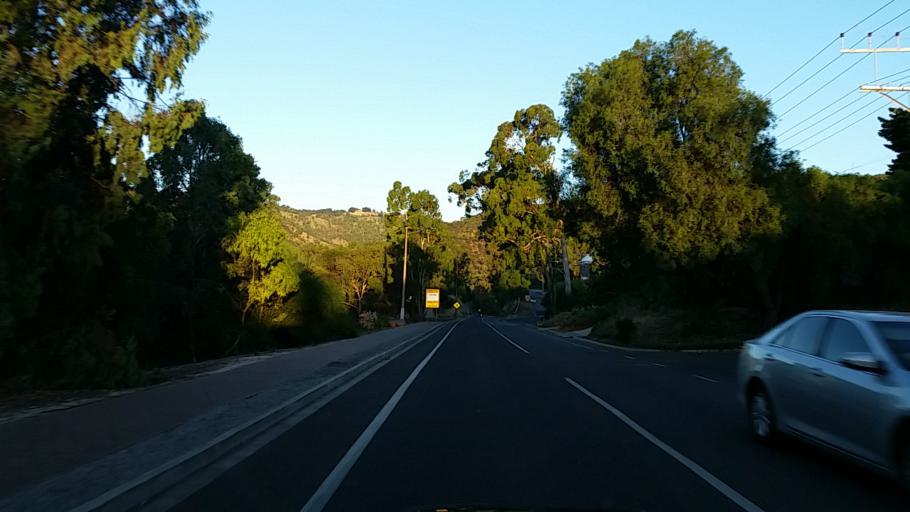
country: AU
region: South Australia
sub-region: Campbelltown
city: Athelstone
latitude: -34.8642
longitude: 138.7133
